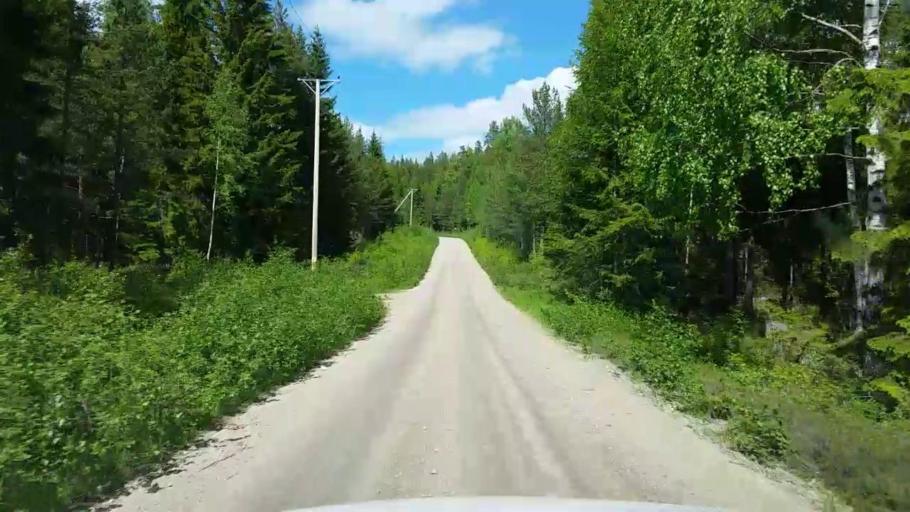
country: SE
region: Gaevleborg
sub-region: Ovanakers Kommun
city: Edsbyn
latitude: 61.5391
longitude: 15.9589
